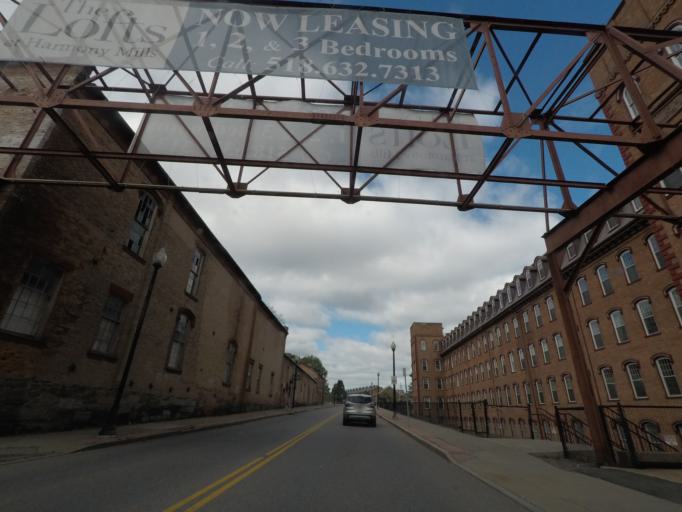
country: US
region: New York
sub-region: Albany County
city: Cohoes
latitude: 42.7818
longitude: -73.7056
